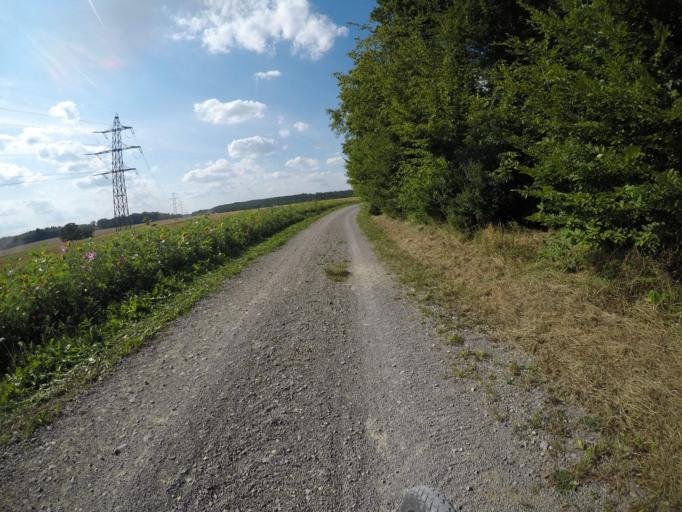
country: DE
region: Baden-Wuerttemberg
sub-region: Regierungsbezirk Stuttgart
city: Altdorf
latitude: 48.6536
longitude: 8.9846
